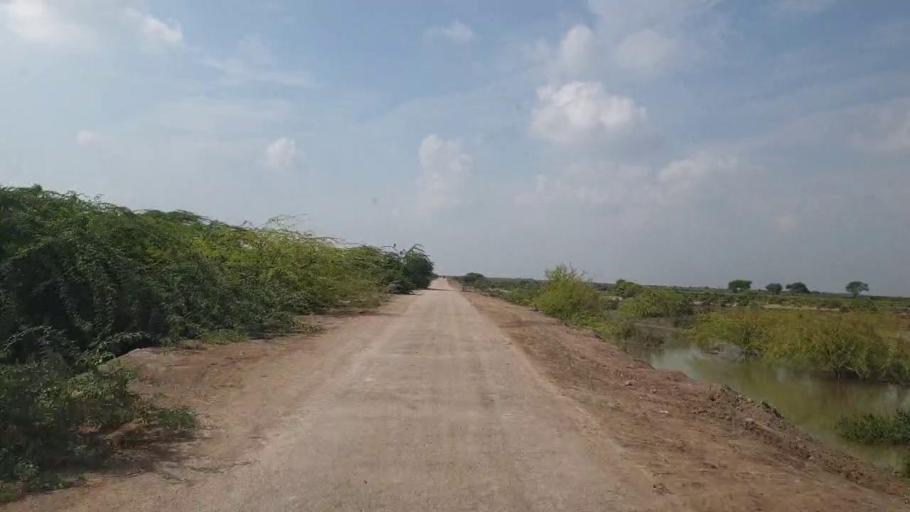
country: PK
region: Sindh
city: Badin
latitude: 24.5065
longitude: 68.6190
